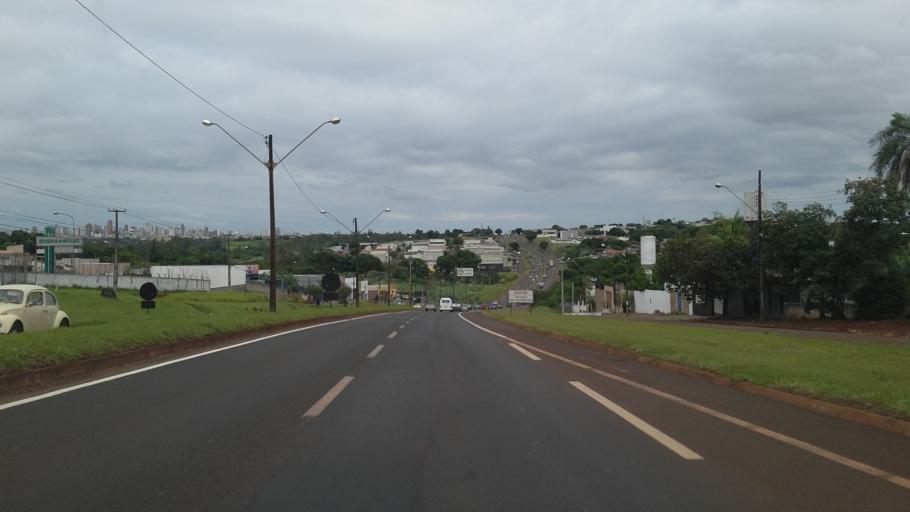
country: BR
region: Parana
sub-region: Londrina
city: Londrina
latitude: -23.2936
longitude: -51.1116
